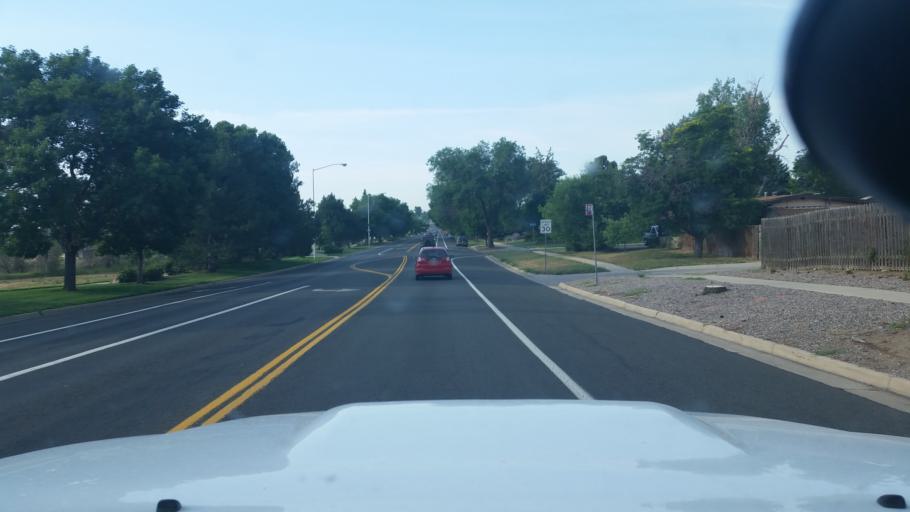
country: US
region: Colorado
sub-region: Broomfield County
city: Broomfield
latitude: 39.9249
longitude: -105.0719
